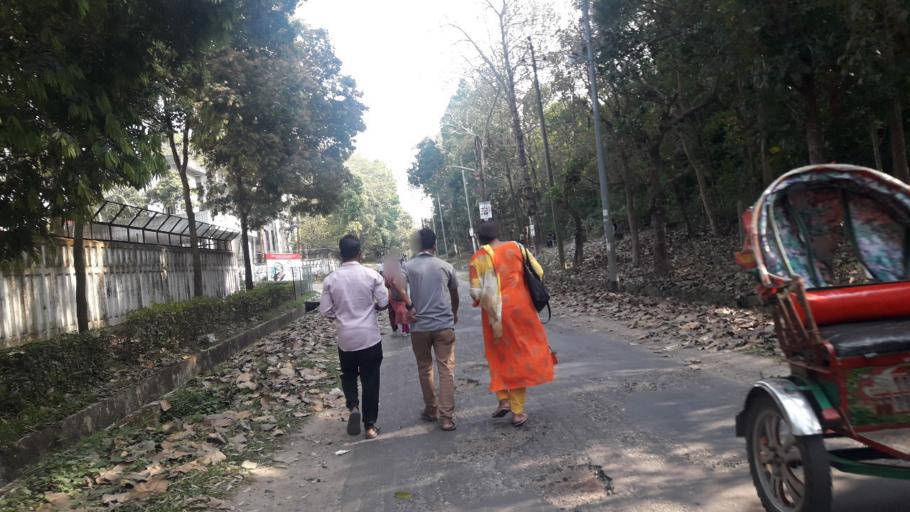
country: BD
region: Chittagong
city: Chittagong
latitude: 22.4681
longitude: 91.7883
